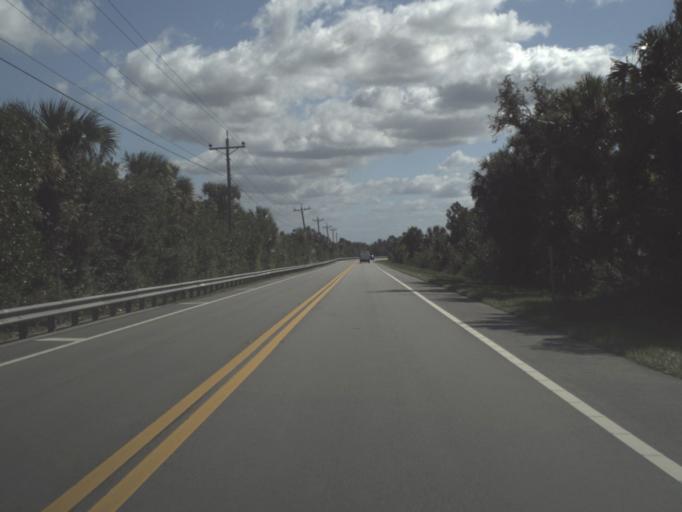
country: US
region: Florida
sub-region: Collier County
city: Marco
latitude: 25.9605
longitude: -81.4999
